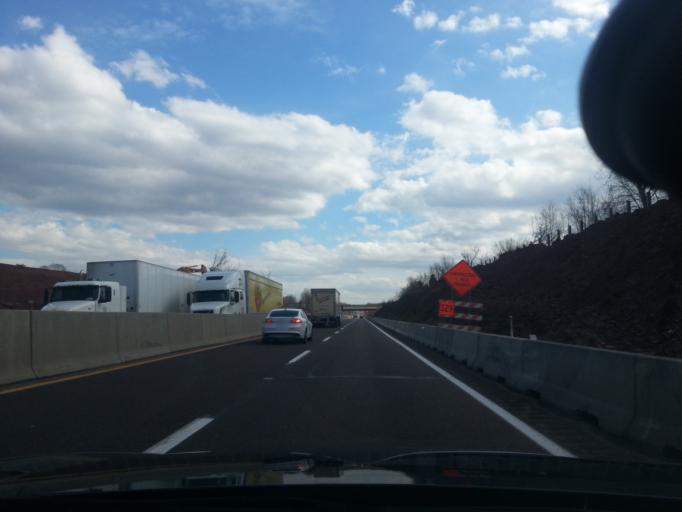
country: US
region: Pennsylvania
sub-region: Montgomery County
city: Kulpsville
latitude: 40.2312
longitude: -75.3362
